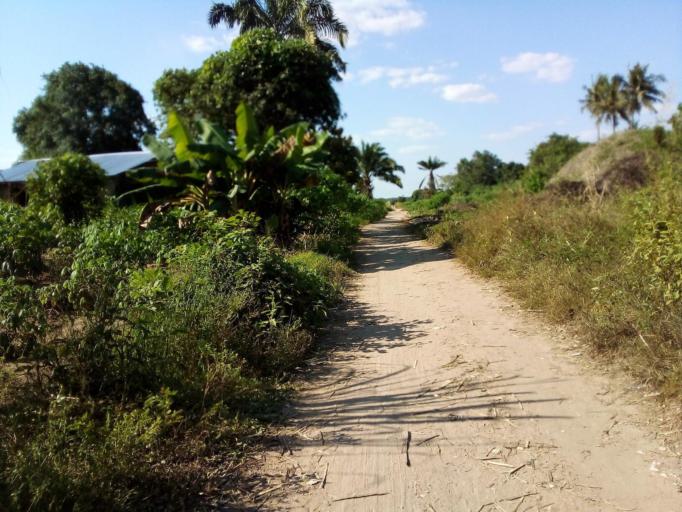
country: MZ
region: Zambezia
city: Quelimane
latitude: -17.5922
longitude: 36.8337
